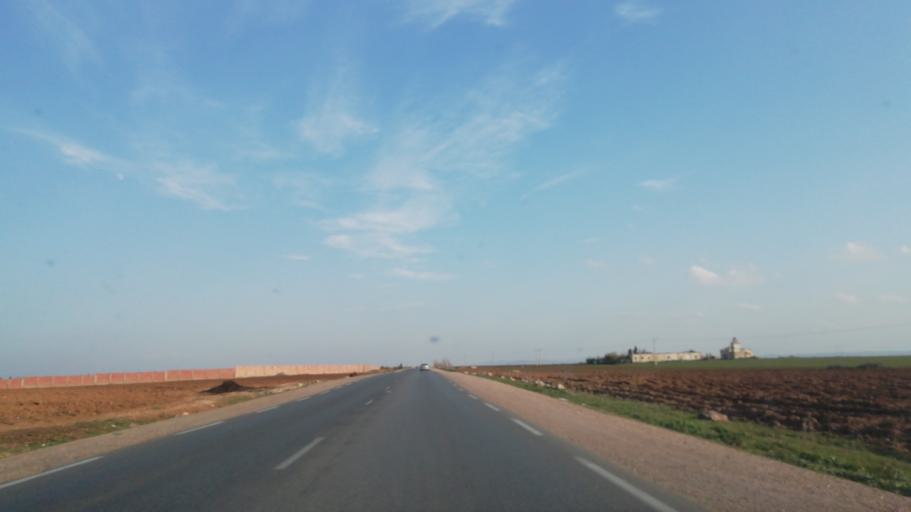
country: DZ
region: Relizane
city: Relizane
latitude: 35.8932
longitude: 0.6126
